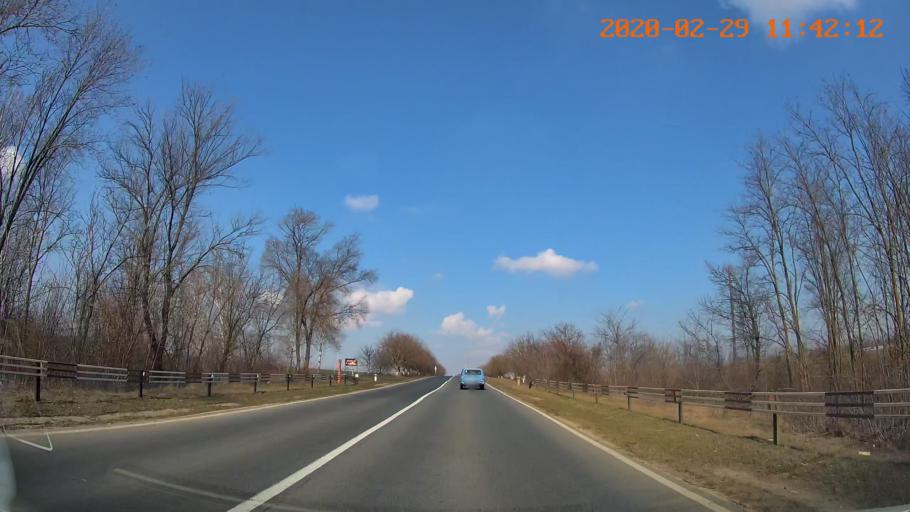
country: MD
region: Rezina
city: Saharna
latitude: 47.6809
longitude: 29.0138
